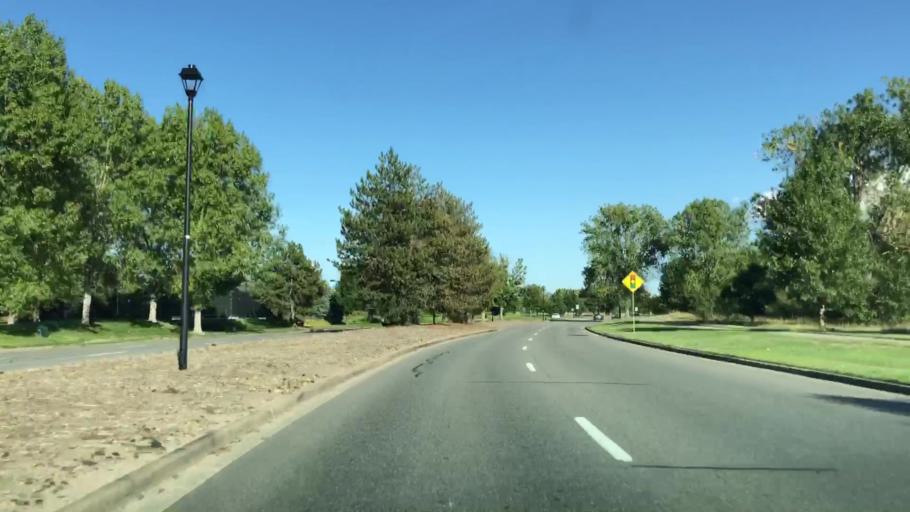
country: US
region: Colorado
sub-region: Arapahoe County
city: Dove Valley
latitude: 39.6111
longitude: -104.8070
